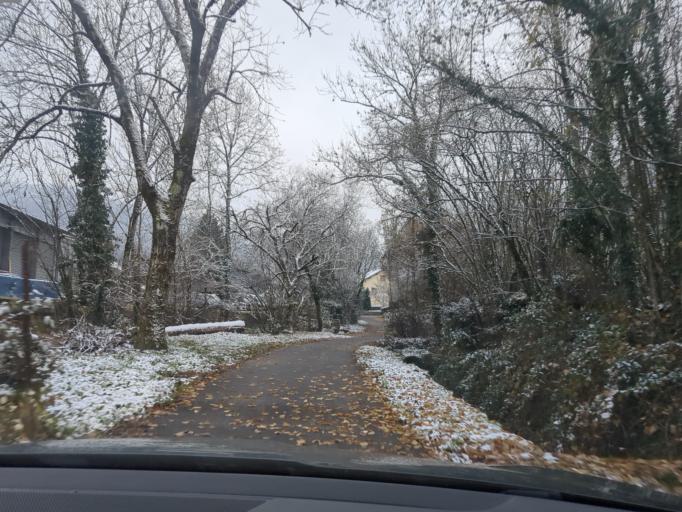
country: FR
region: Franche-Comte
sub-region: Departement du Jura
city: Perrigny
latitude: 46.6583
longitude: 5.5917
